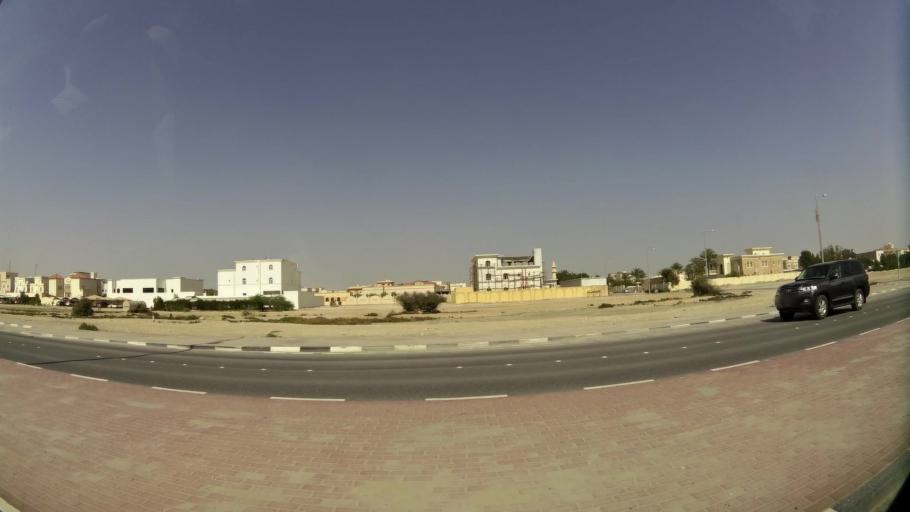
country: QA
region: Baladiyat Umm Salal
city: Umm Salal Muhammad
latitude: 25.3729
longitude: 51.4331
